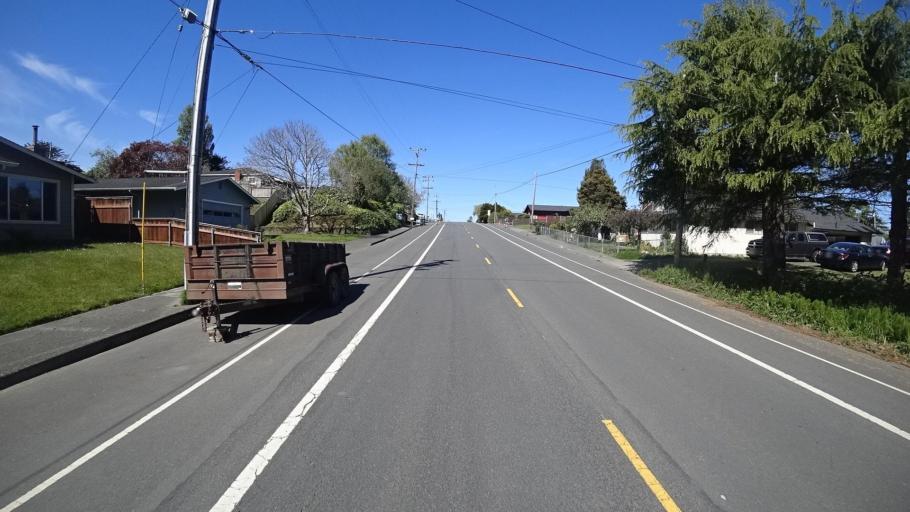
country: US
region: California
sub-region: Humboldt County
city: Myrtletown
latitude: 40.7951
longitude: -124.1278
